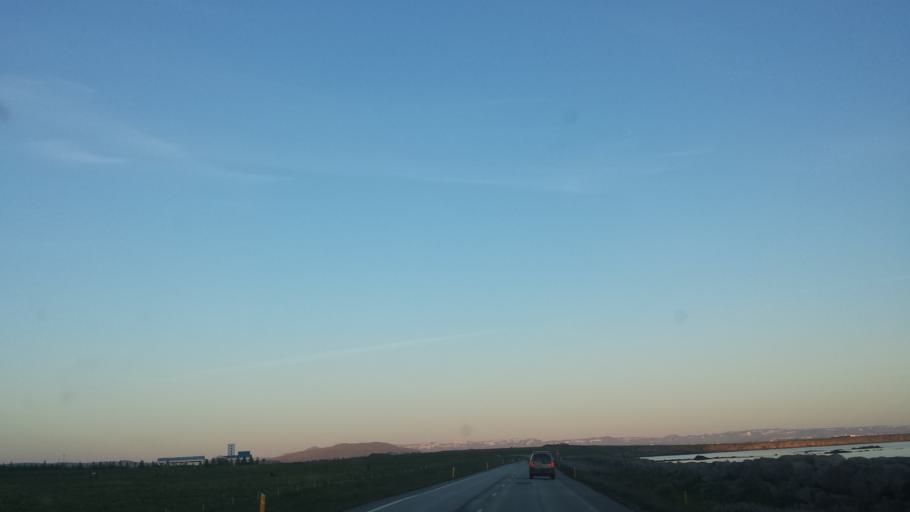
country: IS
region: Capital Region
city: Reykjavik
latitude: 64.2321
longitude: -21.8175
